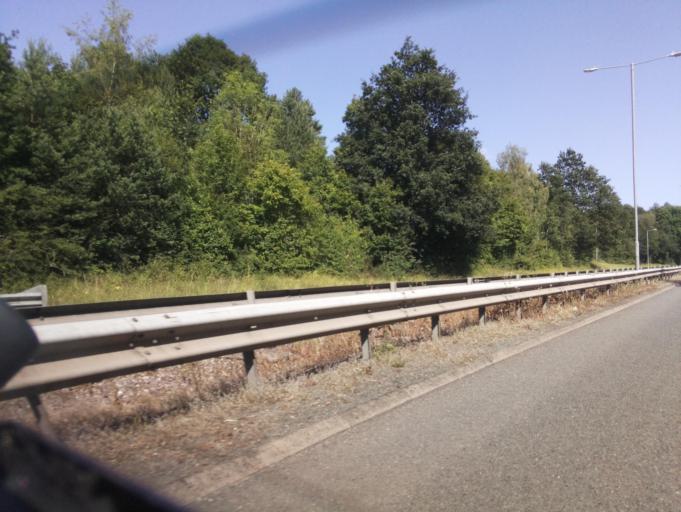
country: GB
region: England
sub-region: Worcestershire
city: Redditch
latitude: 52.2979
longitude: -1.9555
